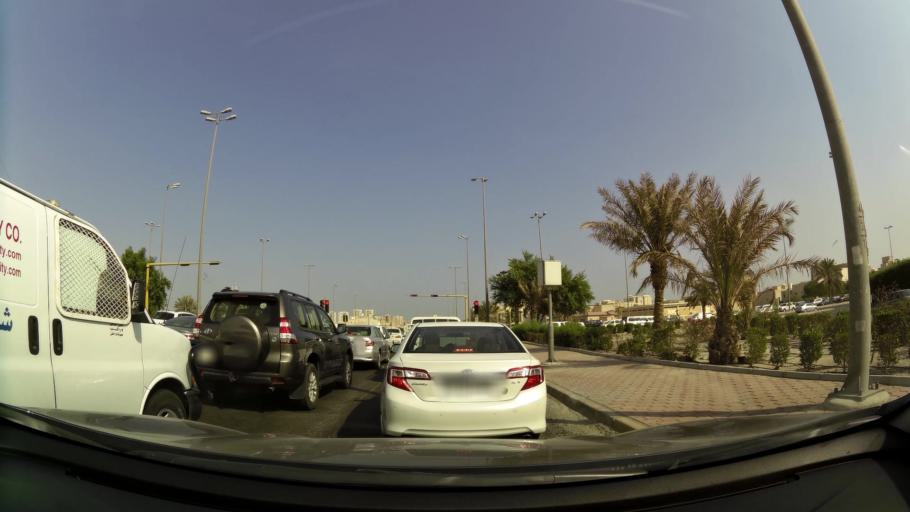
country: KW
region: Al Ahmadi
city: Ar Riqqah
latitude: 29.1340
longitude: 48.1021
